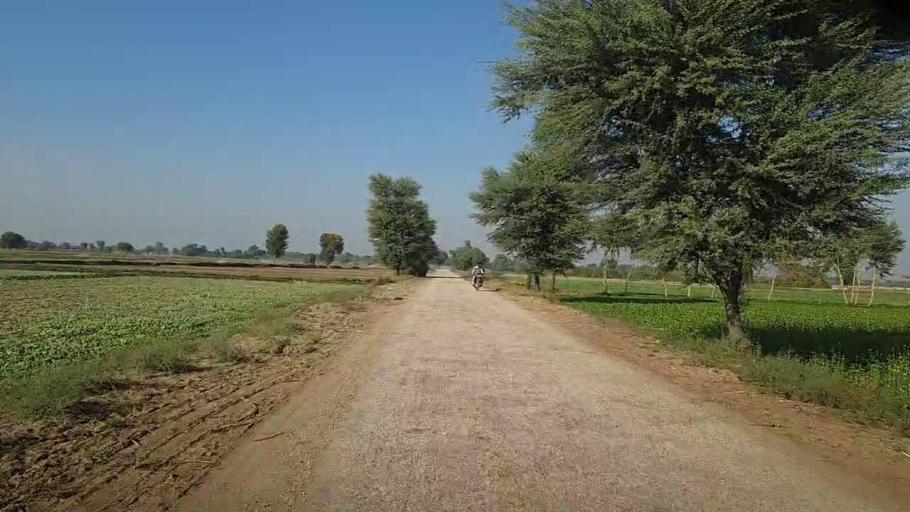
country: PK
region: Sindh
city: Darya Khan Marri
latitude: 26.6841
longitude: 68.3513
